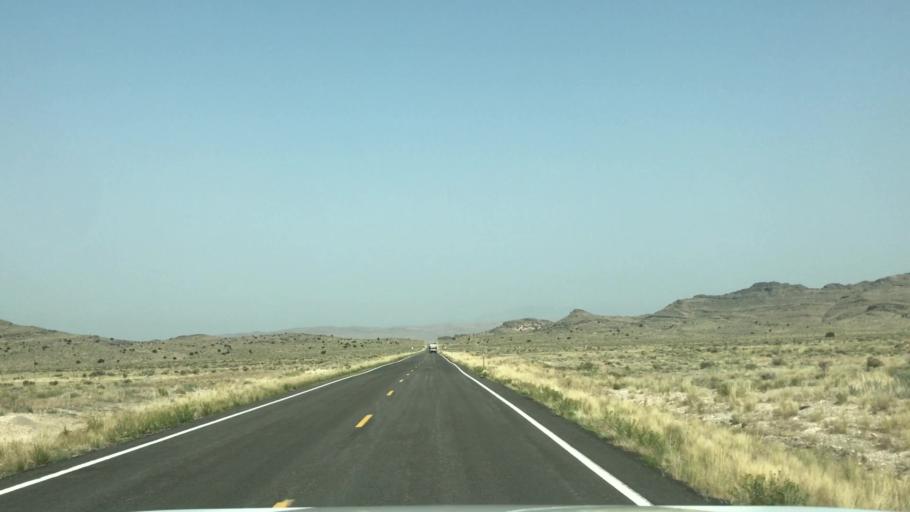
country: US
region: Utah
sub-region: Beaver County
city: Milford
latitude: 39.0763
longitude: -113.6825
